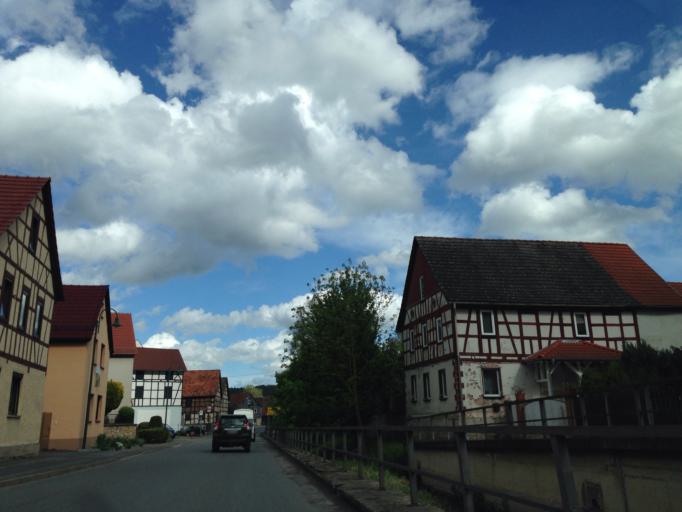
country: DE
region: Thuringia
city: Orlamunde
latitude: 50.7539
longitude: 11.5030
